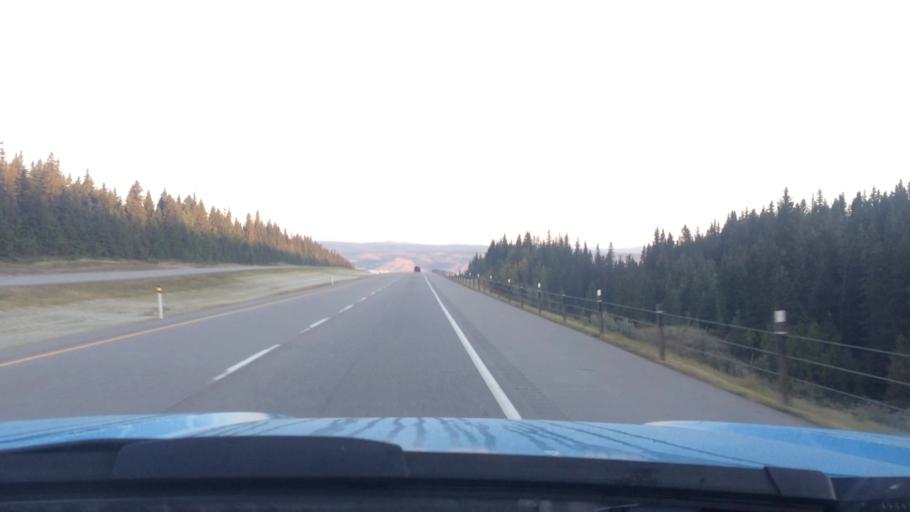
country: CA
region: Alberta
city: Cochrane
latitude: 51.1533
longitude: -114.7439
